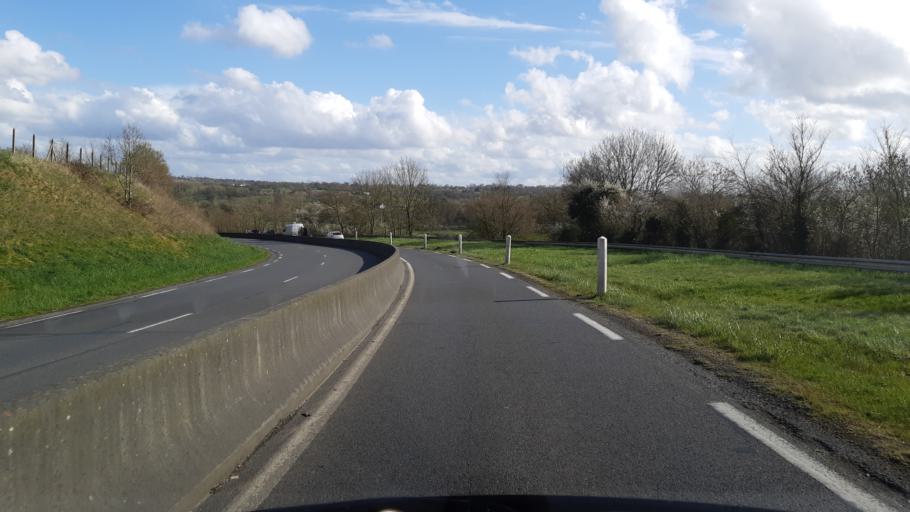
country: FR
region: Lower Normandy
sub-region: Departement de la Manche
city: Agneaux
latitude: 49.0957
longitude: -1.1216
